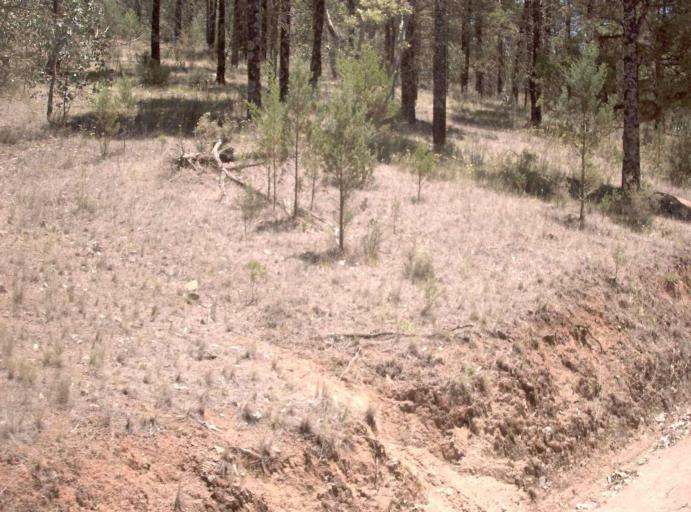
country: AU
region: New South Wales
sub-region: Snowy River
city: Jindabyne
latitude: -36.9007
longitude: 148.4178
